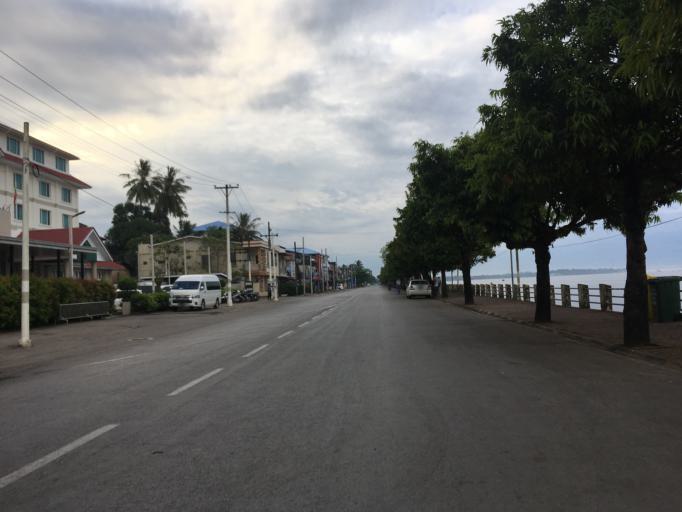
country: MM
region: Mon
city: Mawlamyine
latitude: 16.4786
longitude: 97.6193
